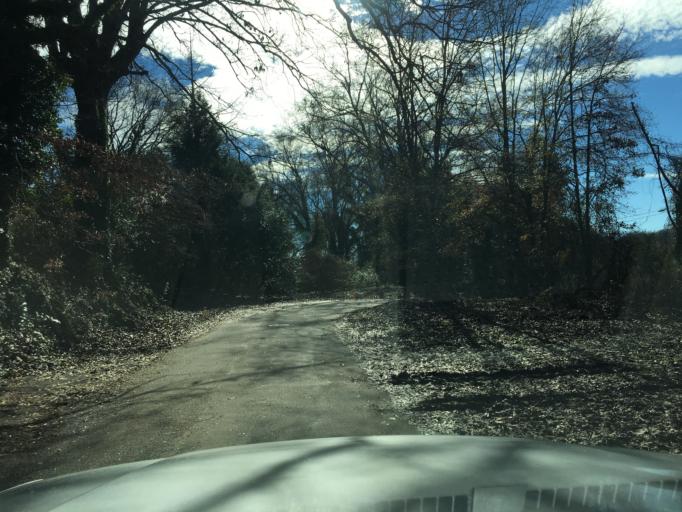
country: US
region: South Carolina
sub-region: Greenville County
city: Greenville
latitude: 34.8572
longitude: -82.3834
